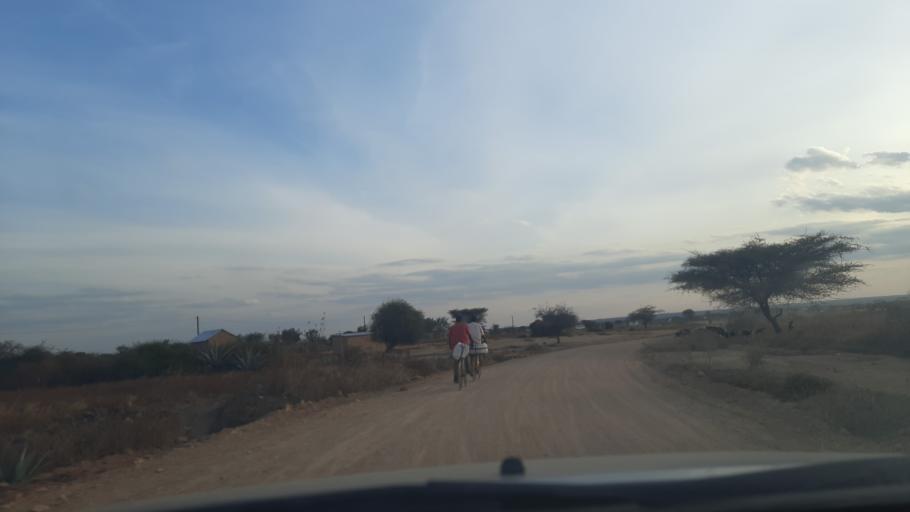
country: TZ
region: Singida
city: Singida
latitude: -4.8319
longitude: 34.7121
